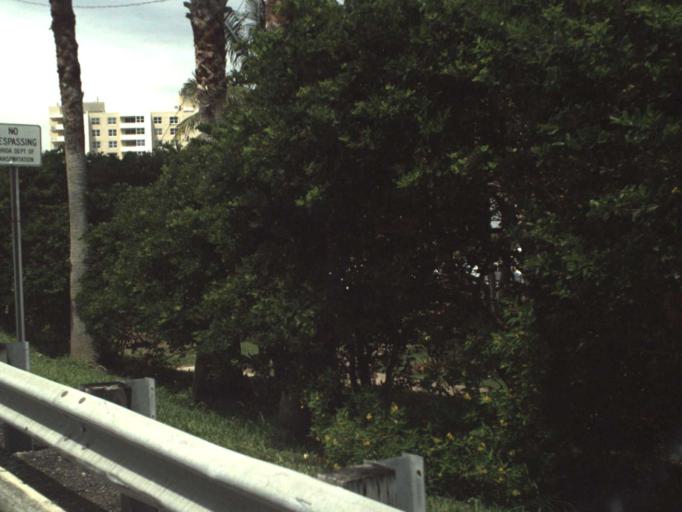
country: US
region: Florida
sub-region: Broward County
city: Lighthouse Point
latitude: 26.2620
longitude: -80.0825
